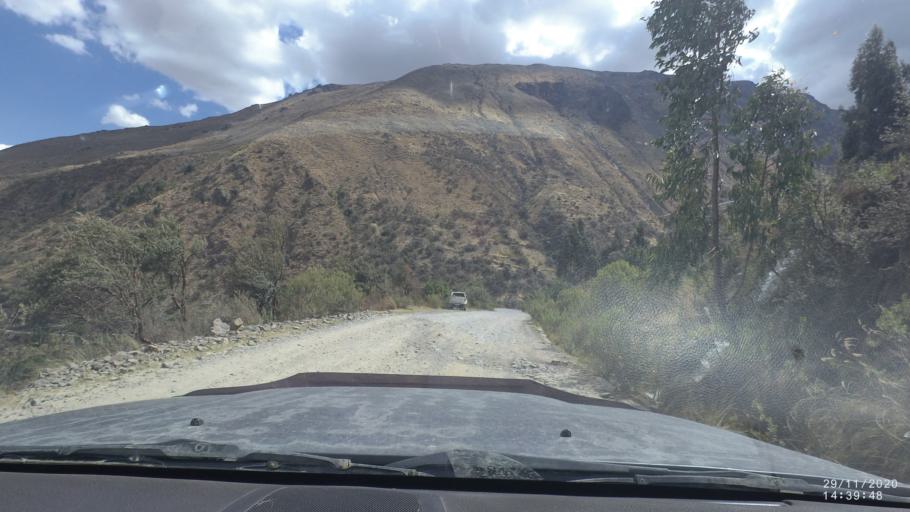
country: BO
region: Cochabamba
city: Sipe Sipe
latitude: -17.2738
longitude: -66.3276
